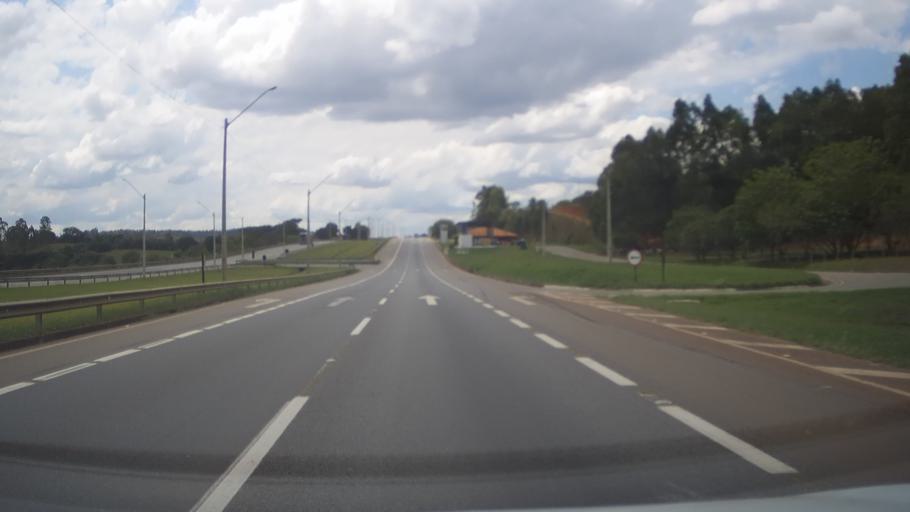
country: BR
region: Minas Gerais
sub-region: Nepomuceno
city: Nepomuceno
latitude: -21.2683
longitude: -45.1369
